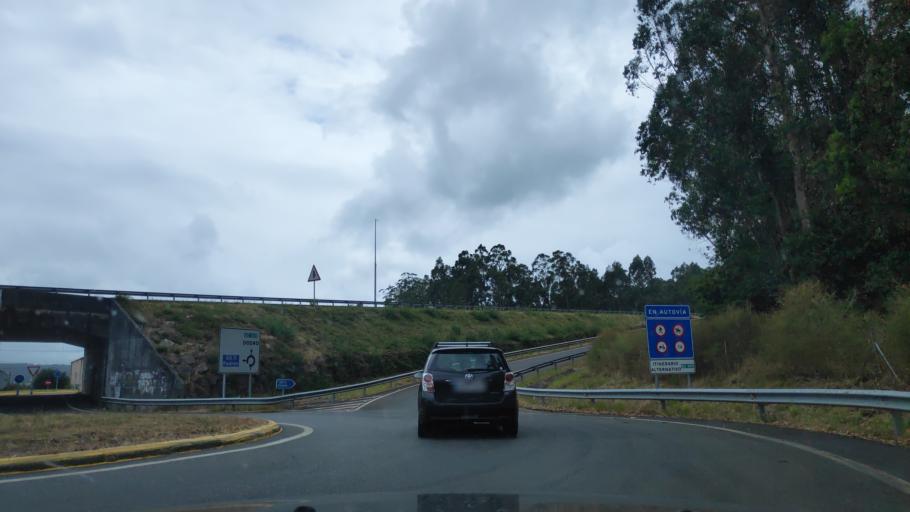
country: ES
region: Galicia
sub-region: Provincia da Coruna
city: Padron
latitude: 42.7266
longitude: -8.6750
